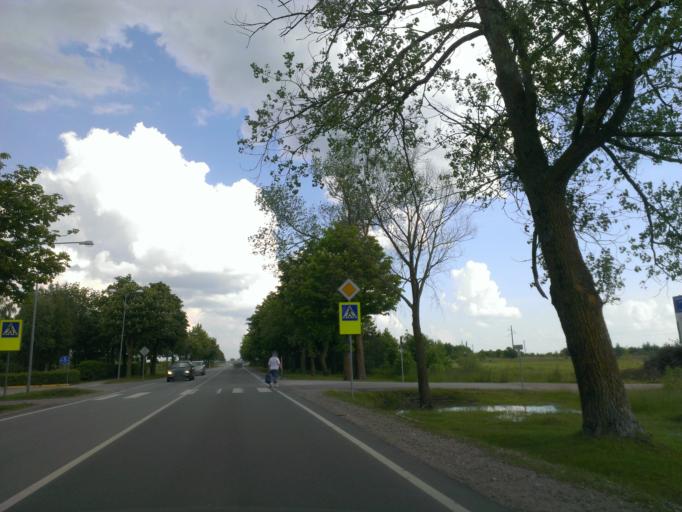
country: LT
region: Klaipedos apskritis
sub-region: Klaipeda
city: Palanga
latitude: 55.9128
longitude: 21.0871
